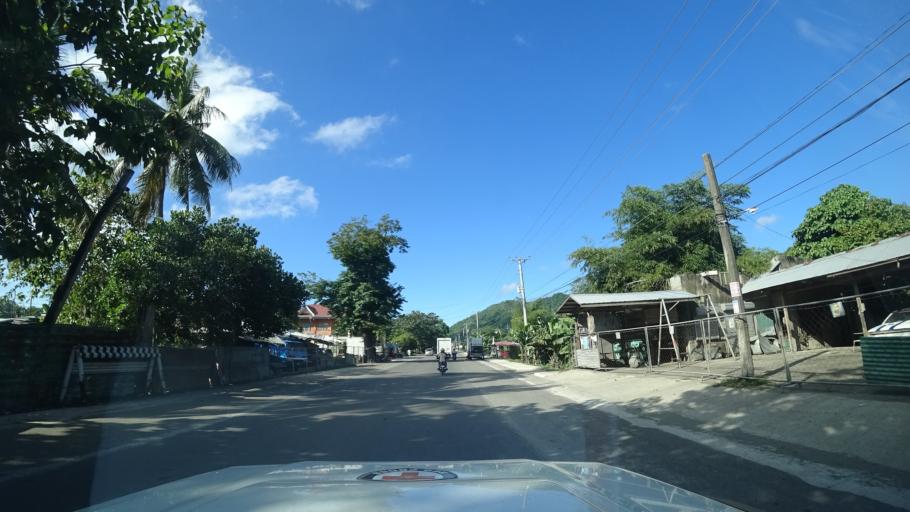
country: PH
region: Eastern Visayas
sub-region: Province of Leyte
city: Pawing
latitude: 11.2135
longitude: 124.9933
